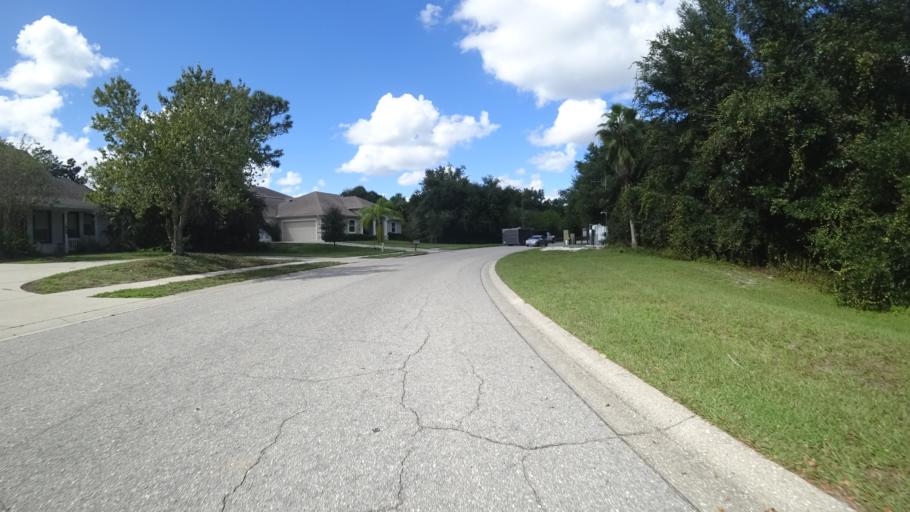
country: US
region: Florida
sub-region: Manatee County
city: Ellenton
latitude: 27.5121
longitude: -82.4051
